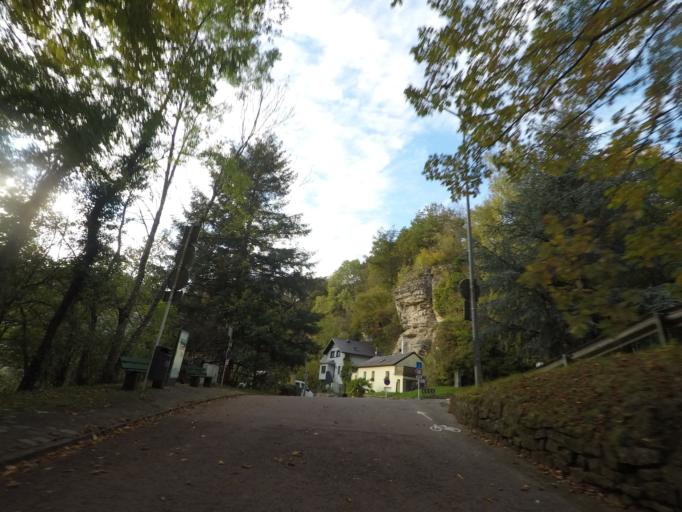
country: LU
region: Luxembourg
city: Kirchberg
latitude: 49.6081
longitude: 6.1645
